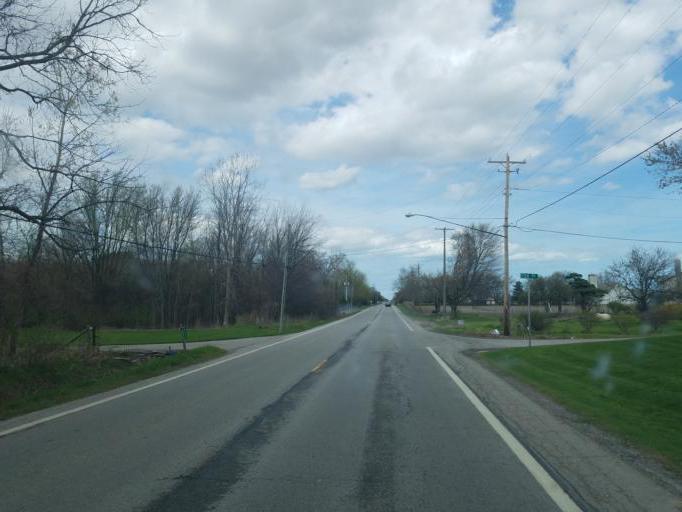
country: US
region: Ohio
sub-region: Erie County
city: Sandusky
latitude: 41.3731
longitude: -82.7437
